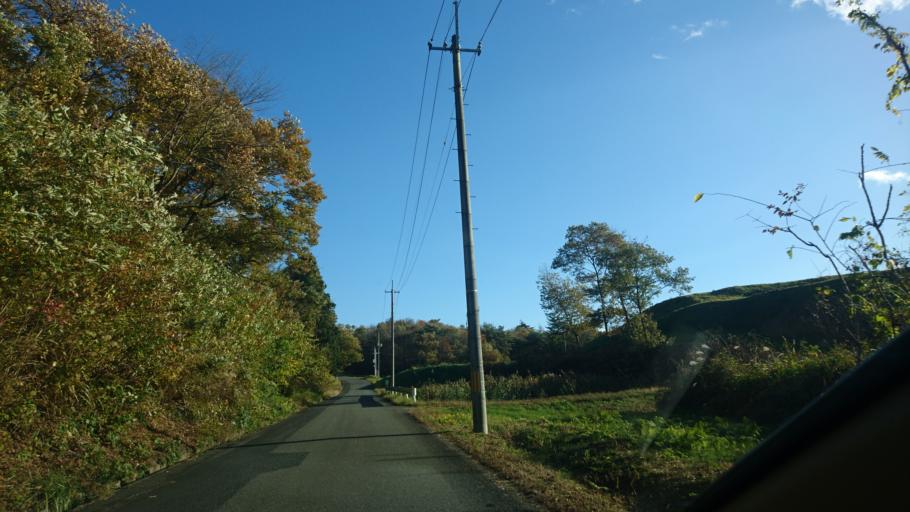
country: JP
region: Iwate
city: Ichinoseki
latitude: 38.9214
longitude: 141.2138
